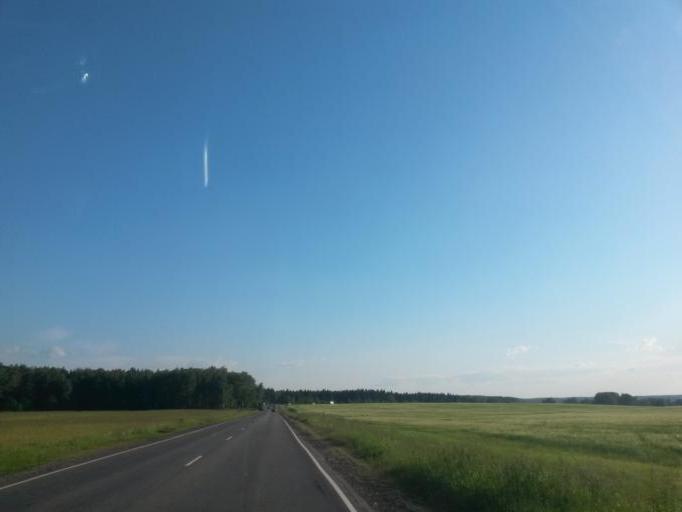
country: RU
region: Moskovskaya
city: Vostryakovo
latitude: 55.3573
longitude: 37.7685
